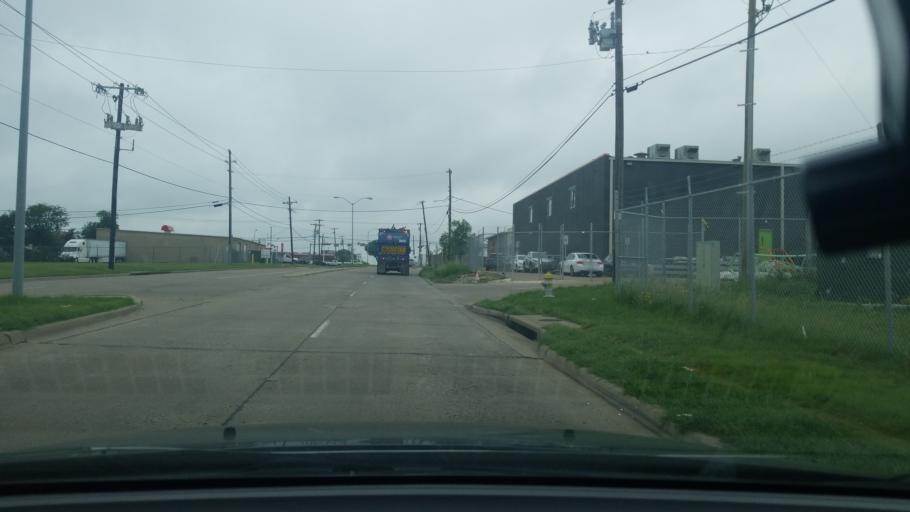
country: US
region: Texas
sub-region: Dallas County
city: Balch Springs
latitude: 32.7781
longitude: -96.6805
